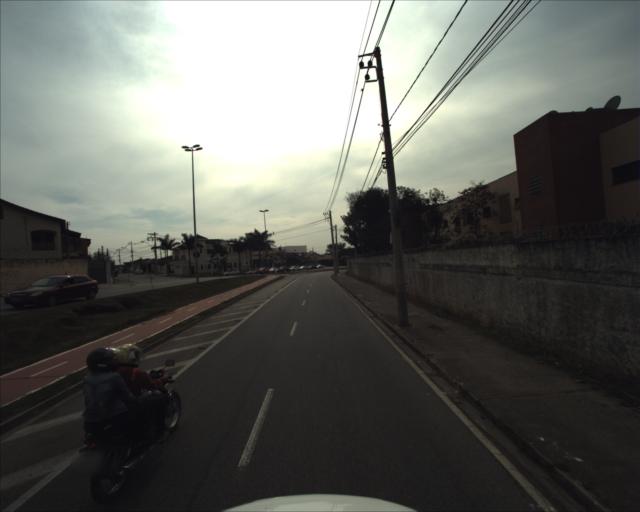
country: BR
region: Sao Paulo
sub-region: Sorocaba
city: Sorocaba
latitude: -23.4757
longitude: -47.4554
